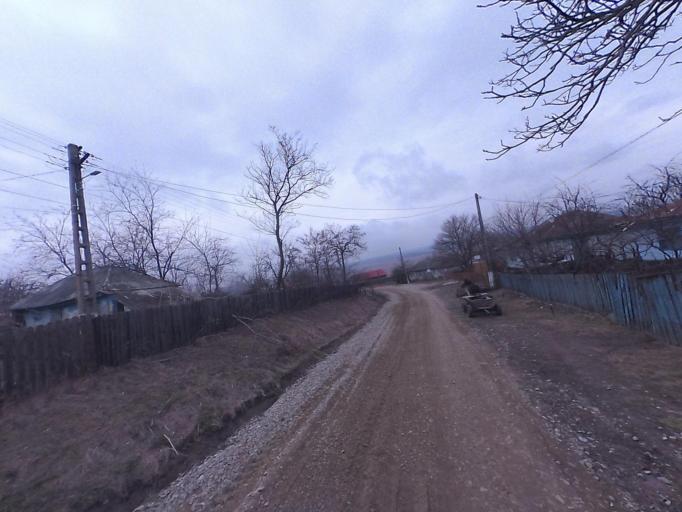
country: RO
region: Iasi
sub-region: Comuna Popricani
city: Popricani
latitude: 47.2946
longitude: 27.5004
